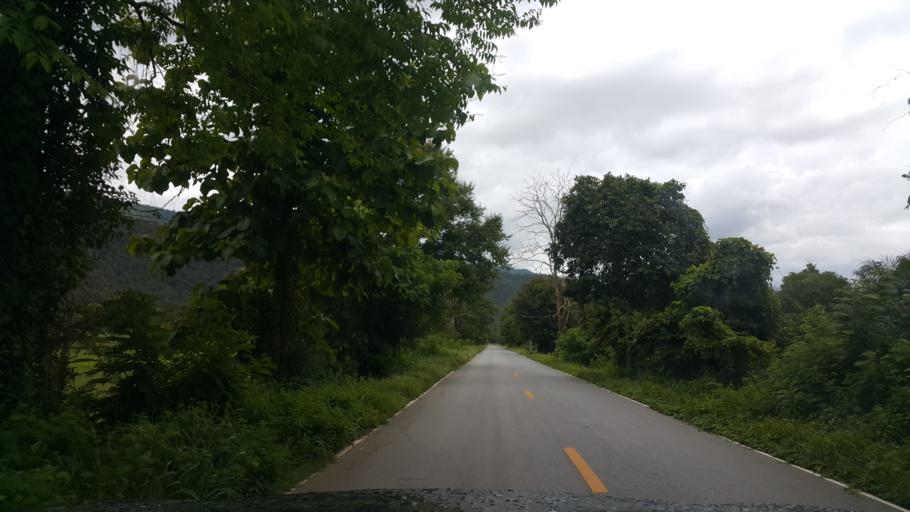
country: TH
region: Phitsanulok
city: Chat Trakan
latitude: 17.3080
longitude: 100.6701
